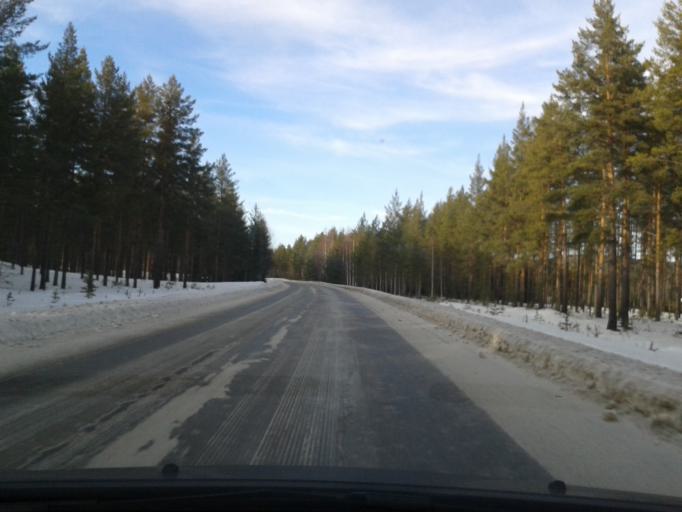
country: SE
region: Vaesternorrland
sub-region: OErnskoeldsviks Kommun
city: Bredbyn
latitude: 63.5362
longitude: 17.9651
